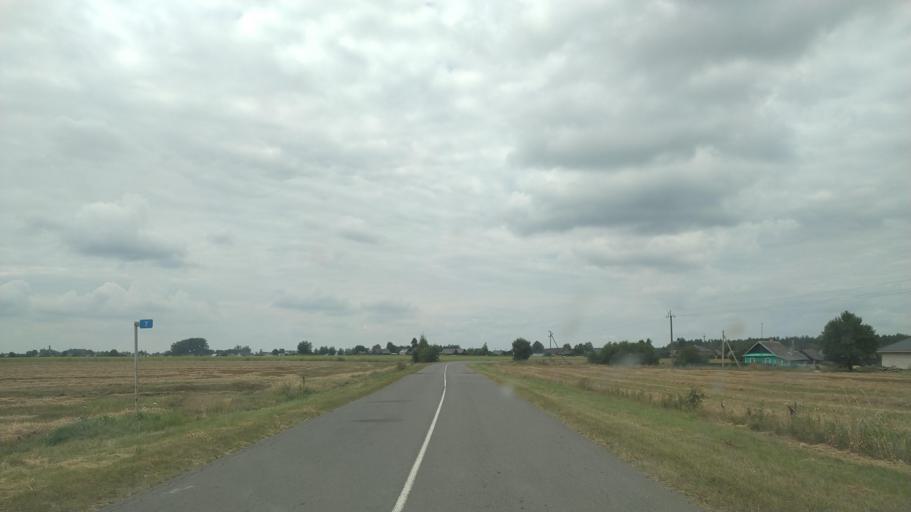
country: BY
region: Brest
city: Byelaazyorsk
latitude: 52.5409
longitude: 25.1151
